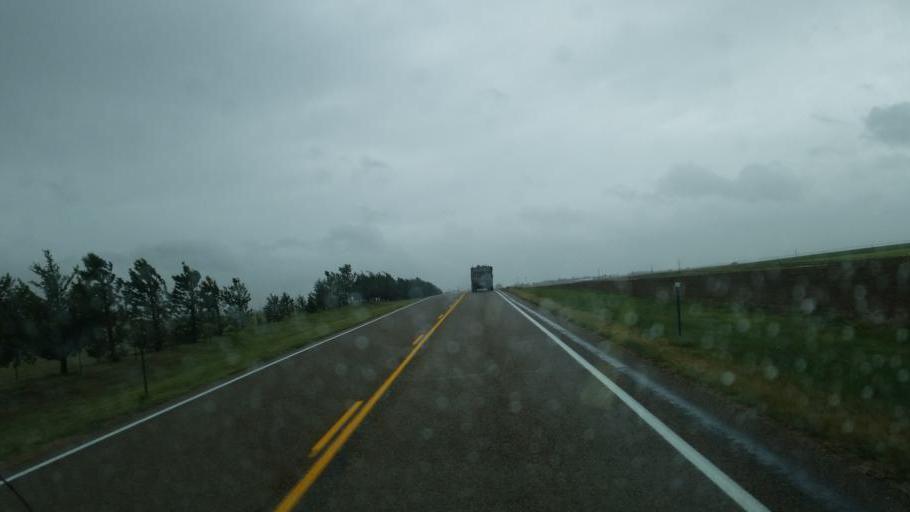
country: US
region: Colorado
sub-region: Cheyenne County
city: Cheyenne Wells
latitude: 38.8296
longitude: -102.3070
